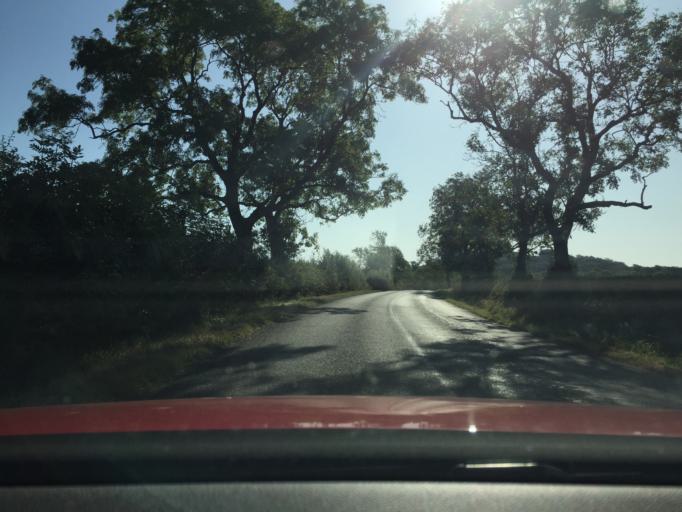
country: GB
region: England
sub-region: Leicestershire
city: Houghton on the Hill
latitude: 52.6400
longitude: -0.9630
